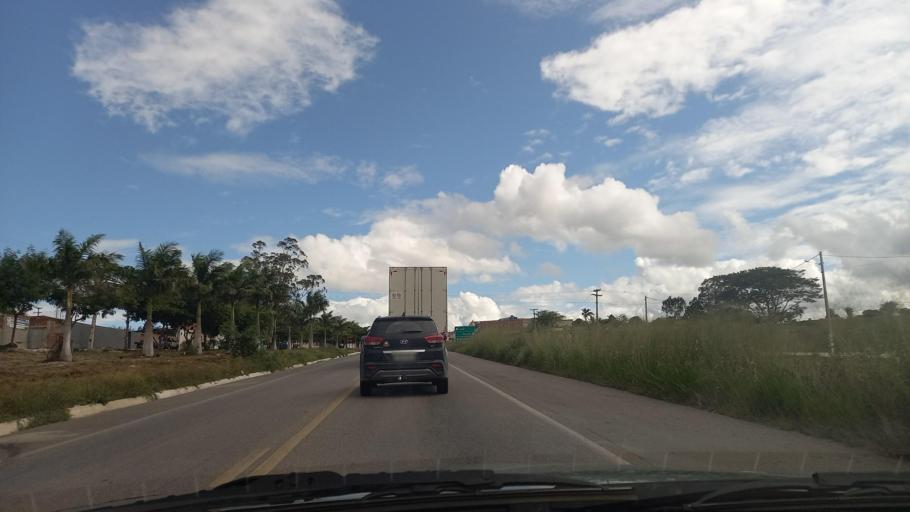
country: BR
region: Pernambuco
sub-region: Lajedo
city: Lajedo
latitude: -8.7066
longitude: -36.4179
